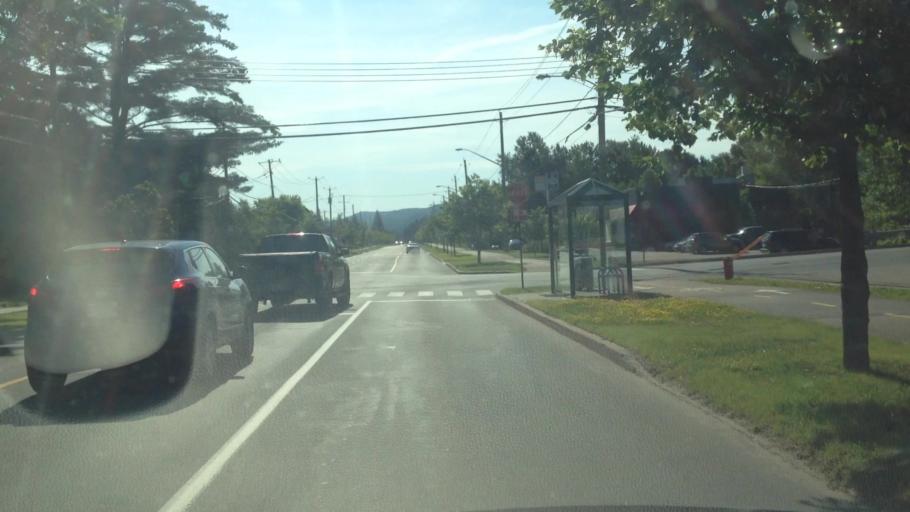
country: CA
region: Quebec
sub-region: Laurentides
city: Mont-Tremblant
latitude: 46.1191
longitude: -74.5718
